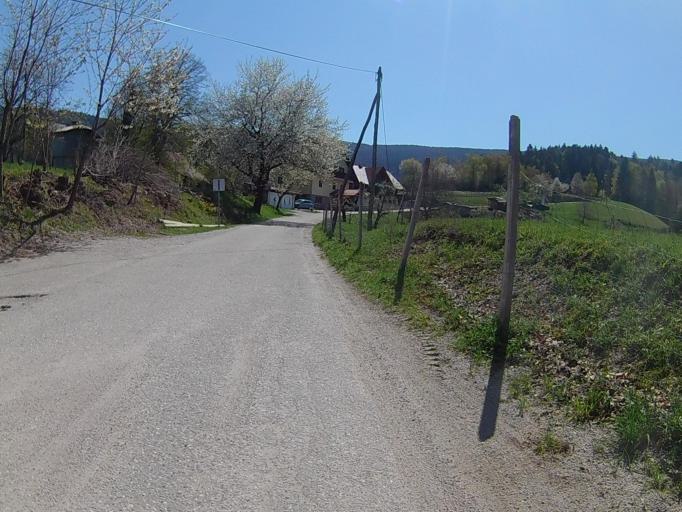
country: SI
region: Ruse
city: Ruse
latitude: 46.5242
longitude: 15.5259
